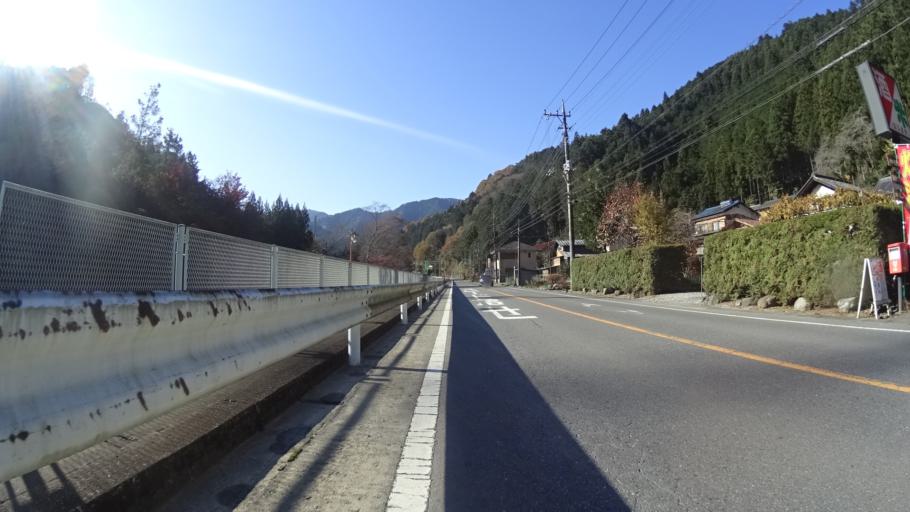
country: JP
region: Tokyo
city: Ome
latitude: 35.8568
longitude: 139.2061
